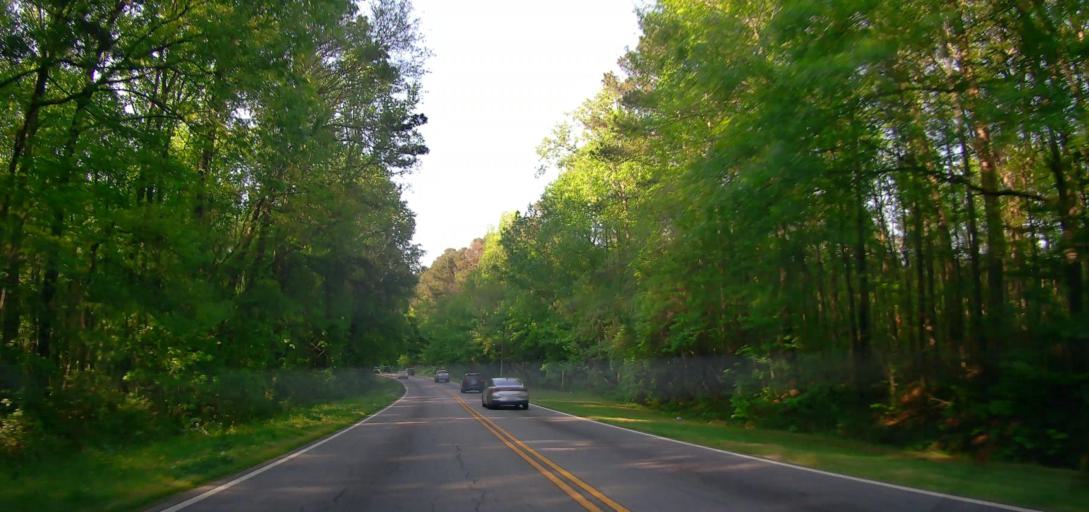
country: US
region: Georgia
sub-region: Newton County
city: Covington
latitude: 33.5956
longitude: -83.8764
